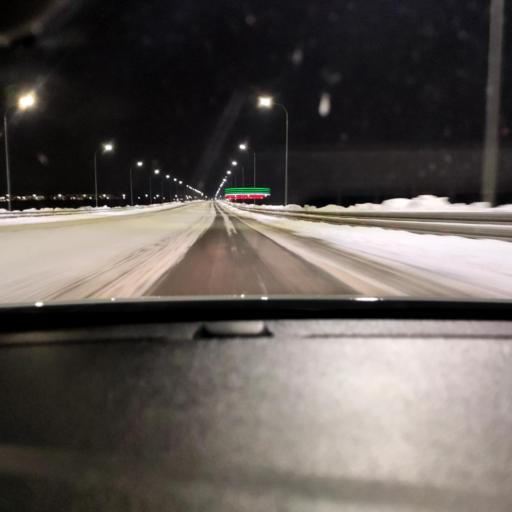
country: RU
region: Tatarstan
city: Sviyazhsk
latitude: 55.7461
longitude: 48.7680
